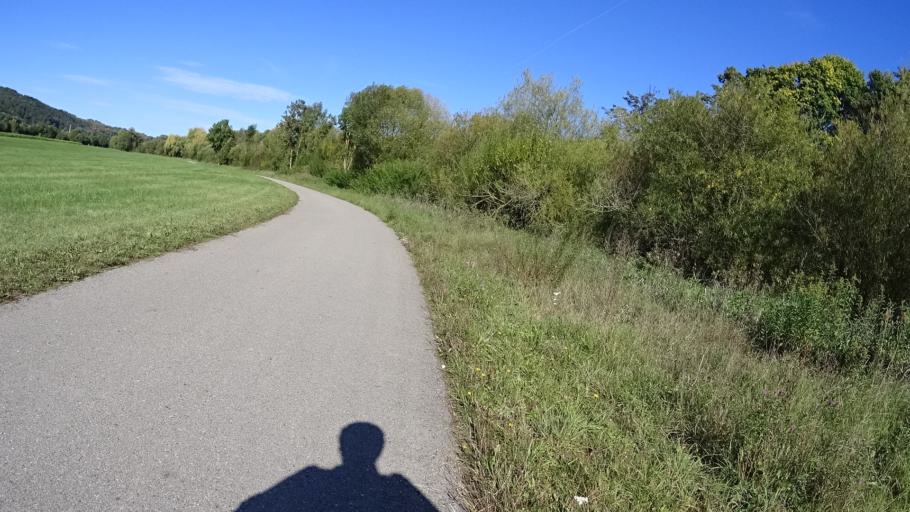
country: DE
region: Bavaria
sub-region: Upper Bavaria
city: Eichstaett
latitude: 48.8790
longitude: 11.2167
